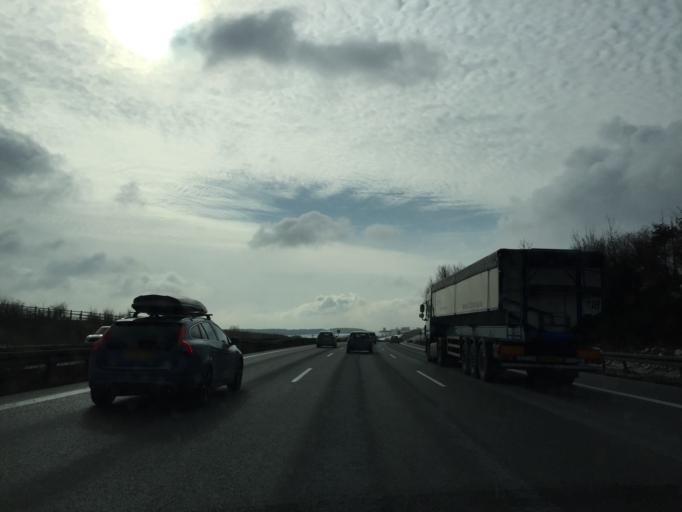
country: DE
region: Bavaria
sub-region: Upper Bavaria
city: Stammham
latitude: 48.8752
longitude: 11.4679
